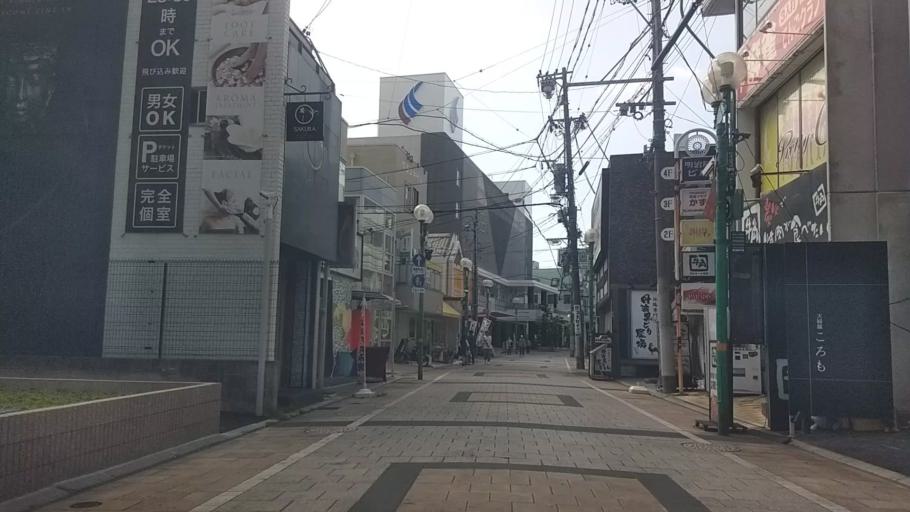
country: JP
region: Shizuoka
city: Hamamatsu
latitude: 34.7045
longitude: 137.7309
